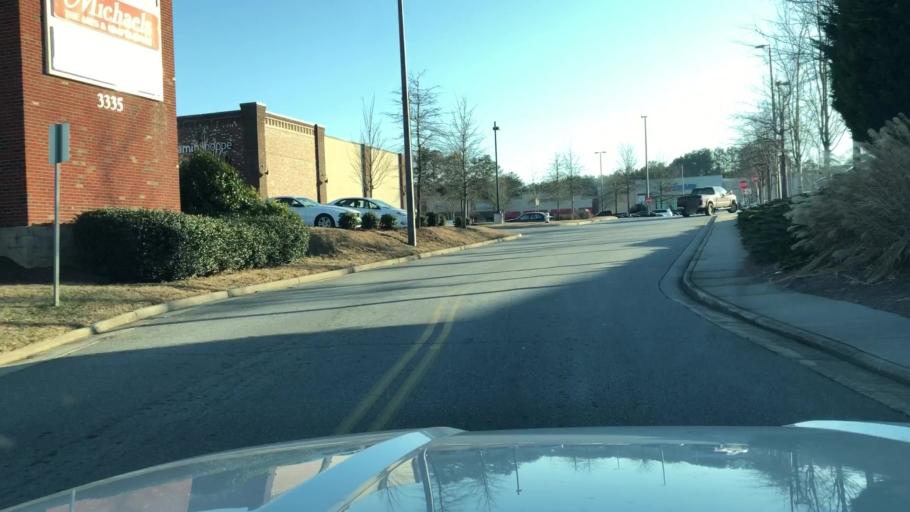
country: US
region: Georgia
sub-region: Cobb County
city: Acworth
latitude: 34.0353
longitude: -84.6822
